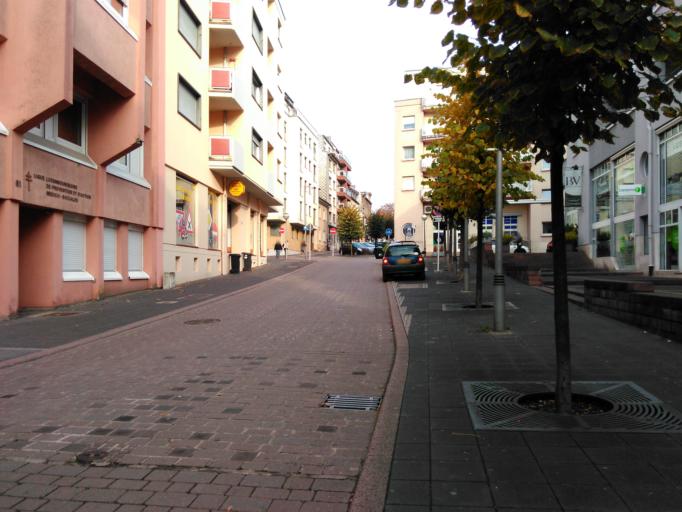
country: LU
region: Luxembourg
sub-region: Canton d'Esch-sur-Alzette
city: Esch-sur-Alzette
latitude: 49.4955
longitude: 5.9821
